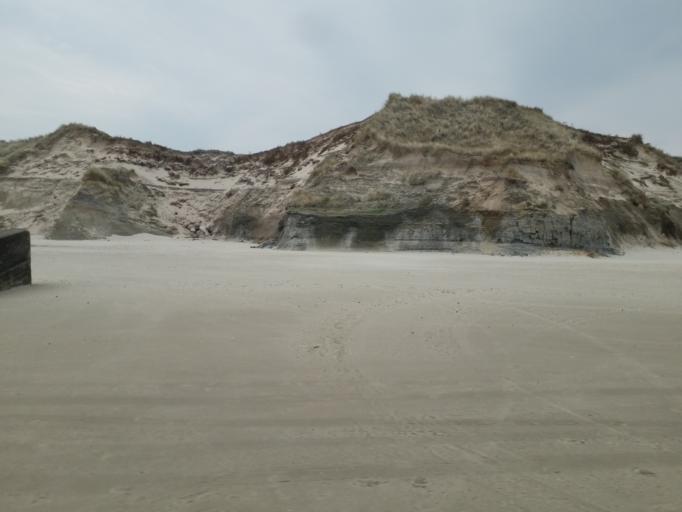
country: DK
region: North Denmark
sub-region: Jammerbugt Kommune
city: Pandrup
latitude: 57.3824
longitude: 9.7189
